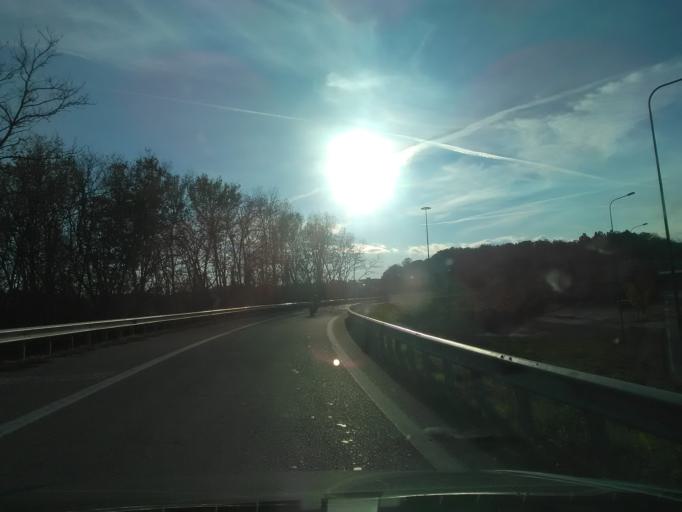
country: IT
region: Piedmont
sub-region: Provincia di Torino
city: Ivrea
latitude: 45.4579
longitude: 7.8847
